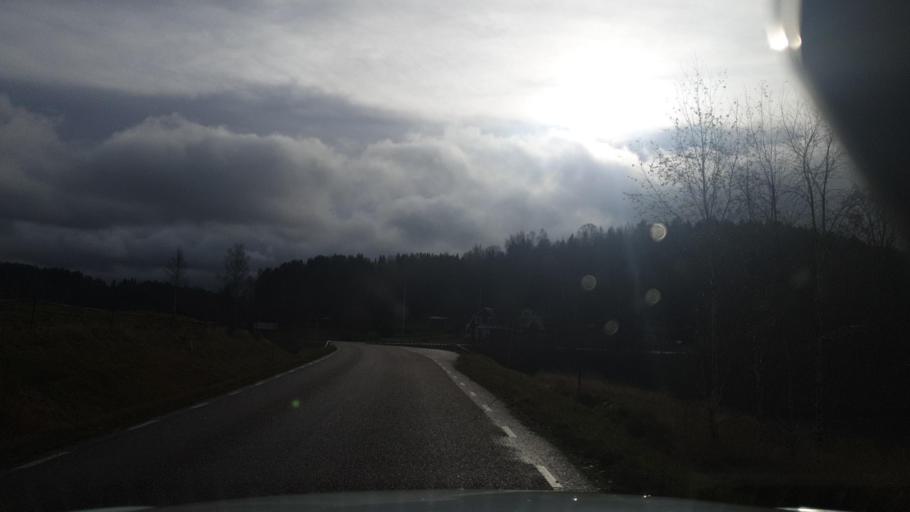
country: NO
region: Ostfold
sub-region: Romskog
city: Romskog
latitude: 59.7017
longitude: 12.0772
